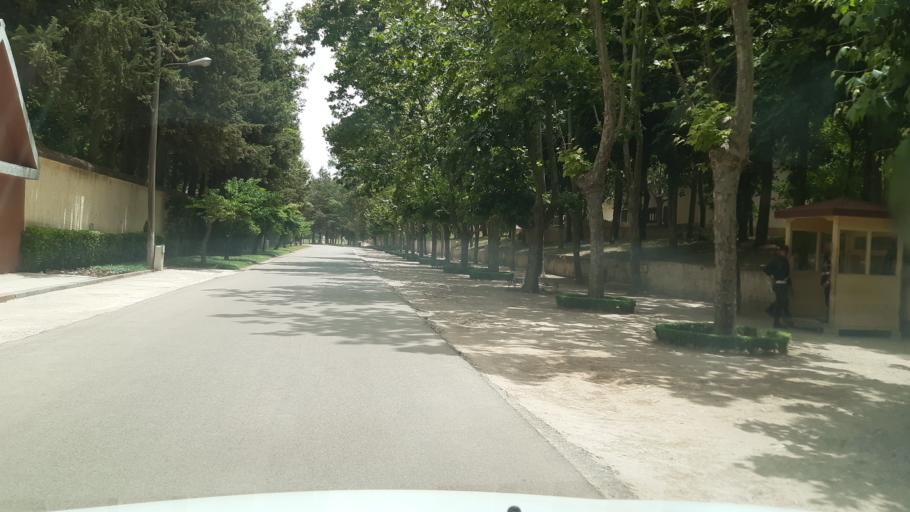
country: MA
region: Meknes-Tafilalet
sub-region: Ifrane
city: Ifrane
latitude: 33.6482
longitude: -5.0339
